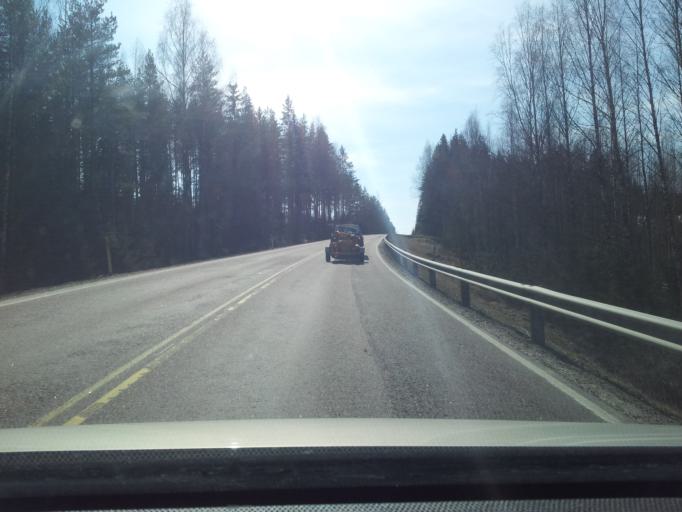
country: FI
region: Kymenlaakso
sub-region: Kotka-Hamina
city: Hamina
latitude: 60.6750
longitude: 27.2757
